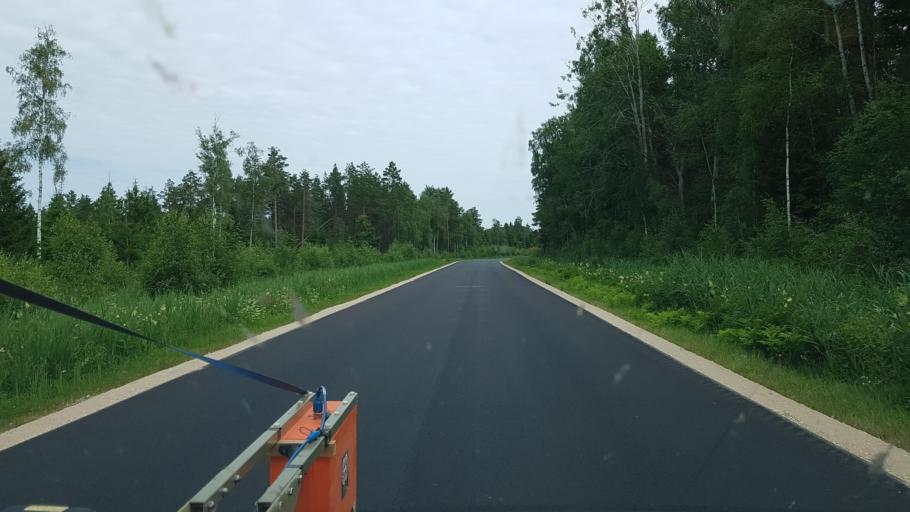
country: EE
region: Paernumaa
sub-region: Audru vald
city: Audru
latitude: 58.6183
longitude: 24.2293
